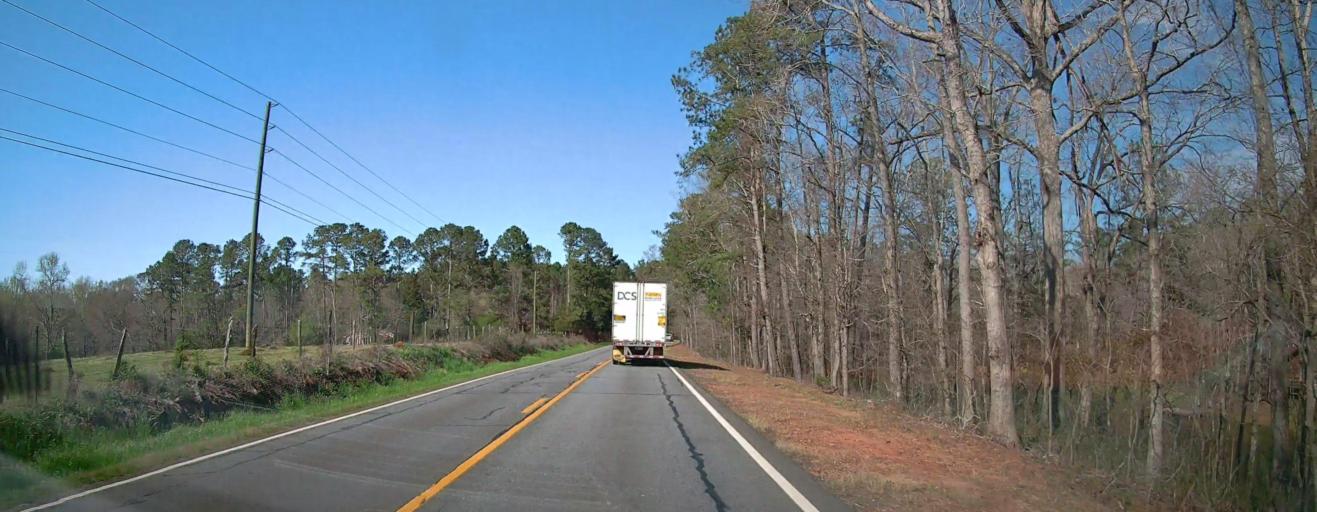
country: US
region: Georgia
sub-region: Monroe County
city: Forsyth
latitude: 33.0848
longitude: -83.9517
